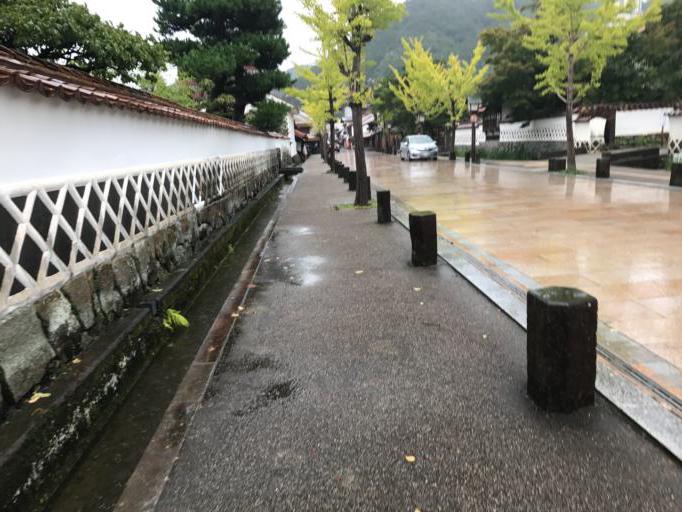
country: JP
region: Shimane
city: Masuda
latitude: 34.4672
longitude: 131.7735
